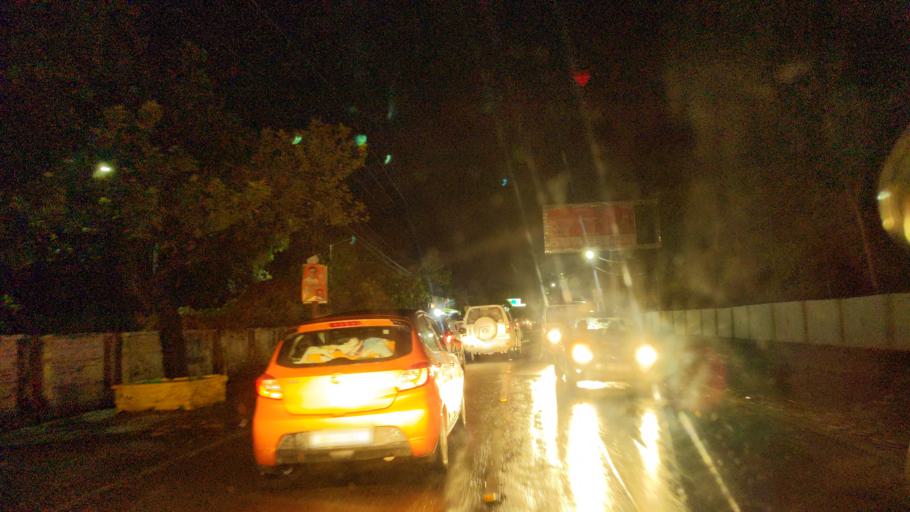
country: IN
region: Uttarakhand
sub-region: Naini Tal
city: Haldwani
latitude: 29.2070
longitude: 79.5204
